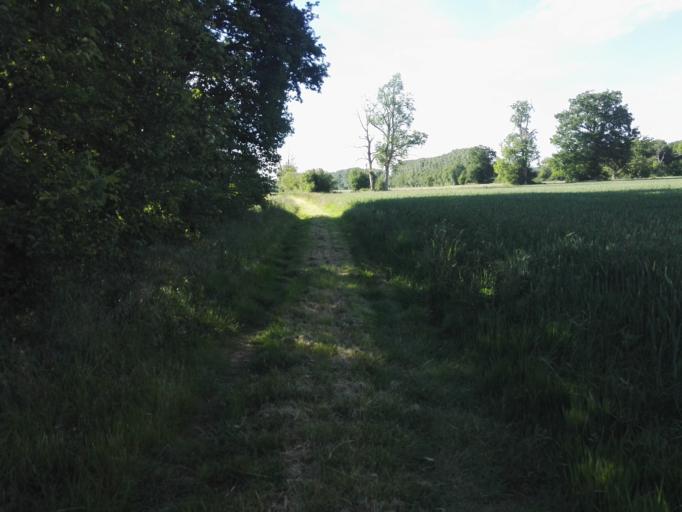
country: FR
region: Haute-Normandie
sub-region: Departement de l'Eure
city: Pacy-sur-Eure
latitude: 48.9907
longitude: 1.3970
